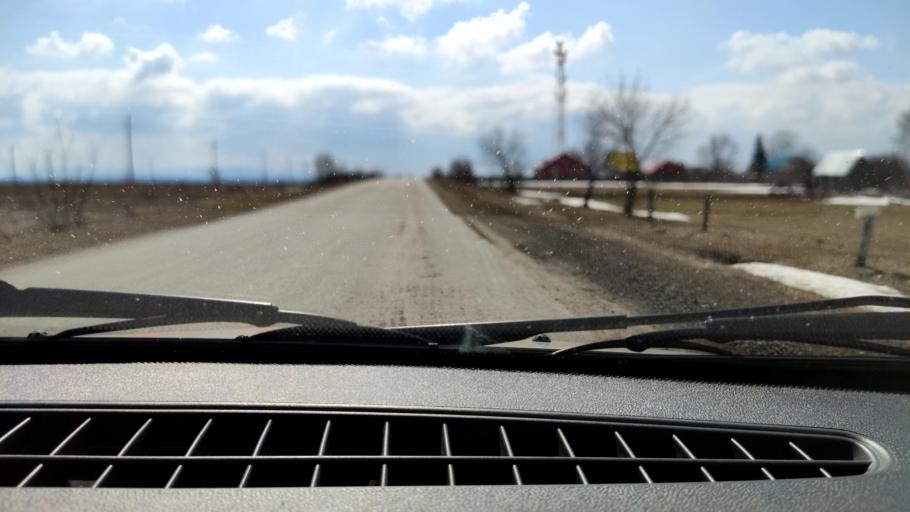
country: RU
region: Bashkortostan
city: Kudeyevskiy
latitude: 54.8465
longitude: 56.7962
